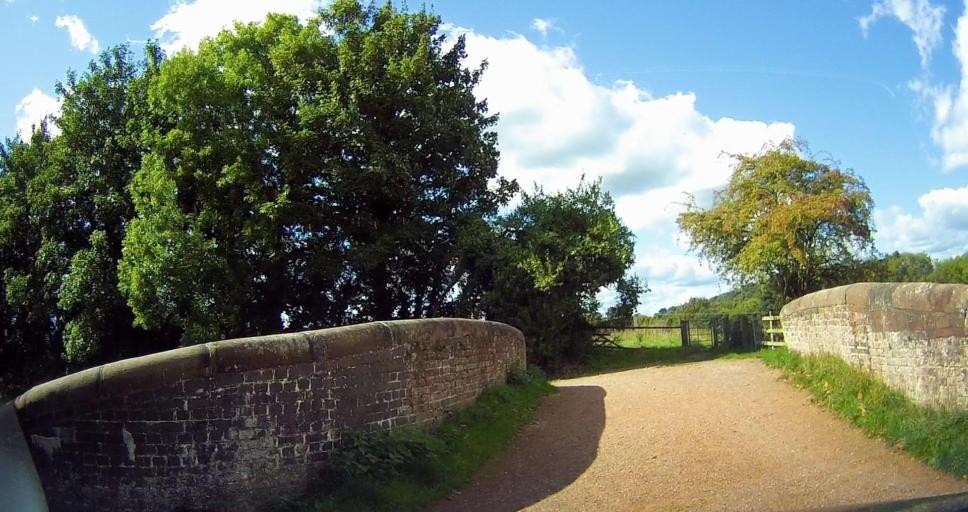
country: GB
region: England
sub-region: Staffordshire
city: Stone
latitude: 52.9153
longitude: -2.1642
